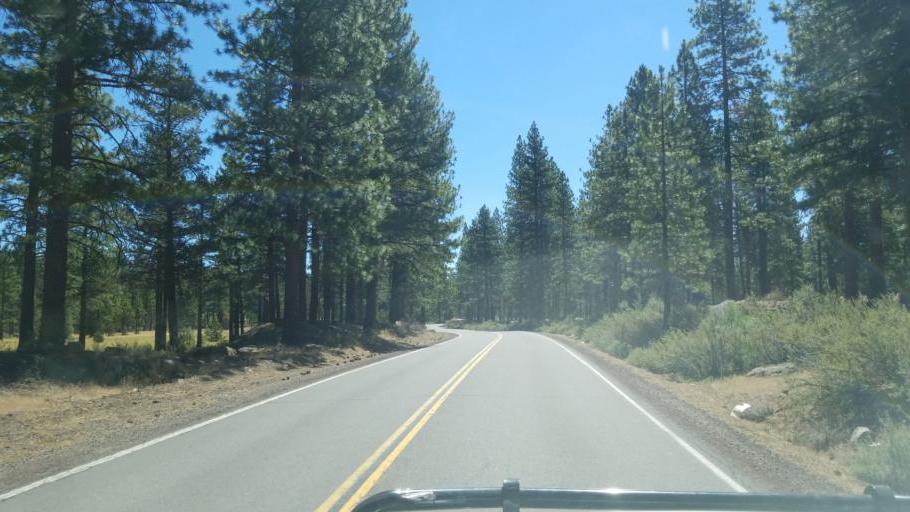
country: US
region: California
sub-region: Lassen County
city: Susanville
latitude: 40.4226
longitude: -120.7160
